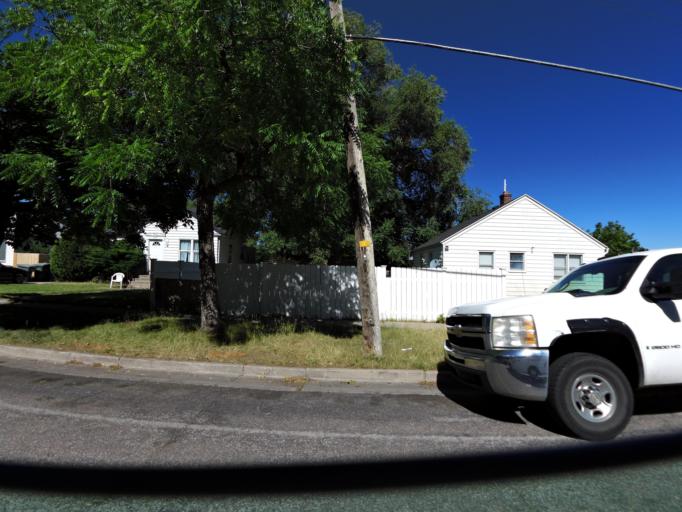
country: US
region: Utah
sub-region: Weber County
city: Ogden
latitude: 41.2242
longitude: -111.9454
